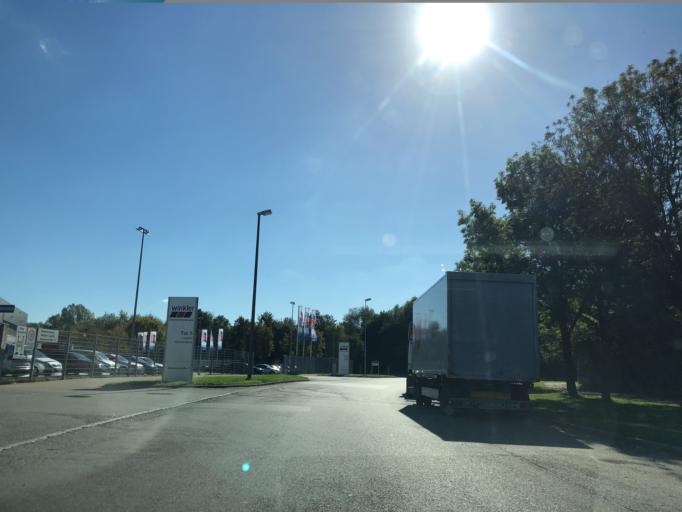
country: DE
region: Baden-Wuerttemberg
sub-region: Tuebingen Region
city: Ulm
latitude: 48.3622
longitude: 9.9551
